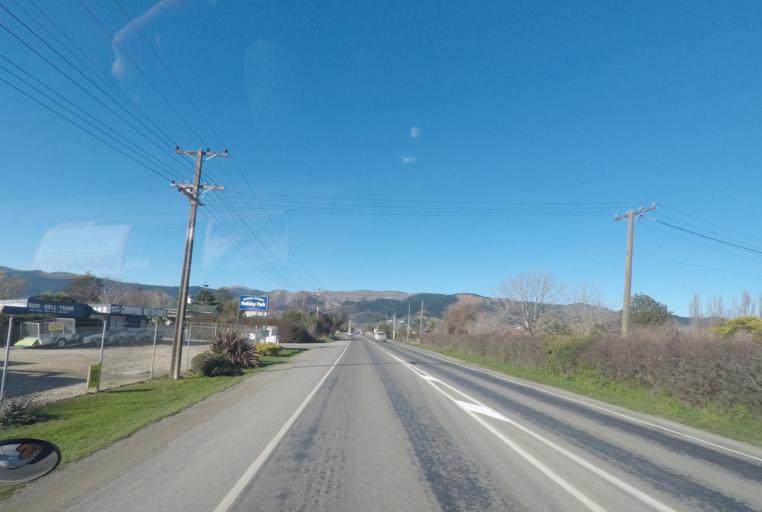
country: NZ
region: Tasman
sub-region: Tasman District
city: Richmond
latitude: -41.3286
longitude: 173.1729
